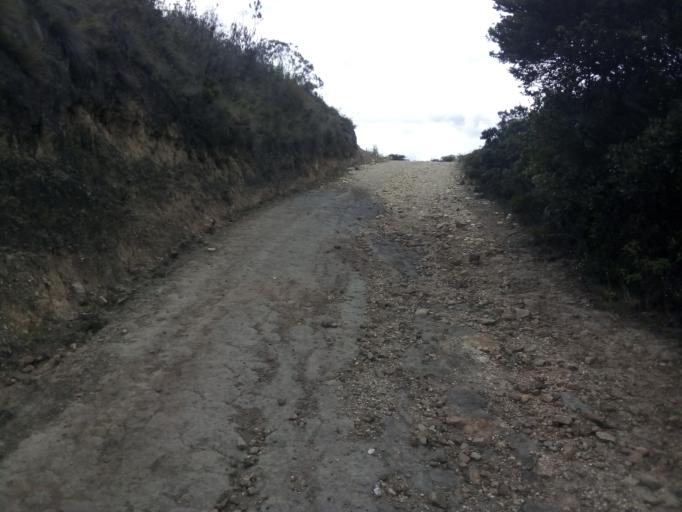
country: CO
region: Boyaca
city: Toca
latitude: 5.5965
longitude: -73.1214
